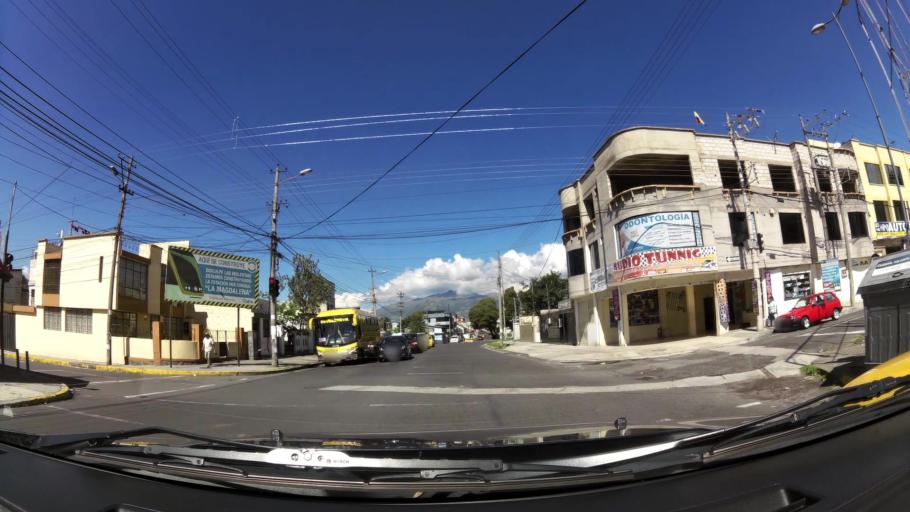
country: EC
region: Pichincha
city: Quito
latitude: -0.2402
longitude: -78.5243
